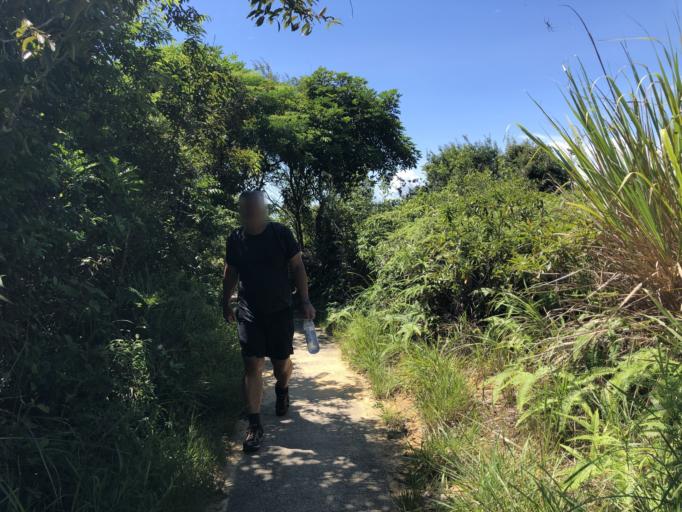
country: HK
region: Tuen Mun
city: Tuen Mun
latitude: 22.2840
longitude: 113.9831
